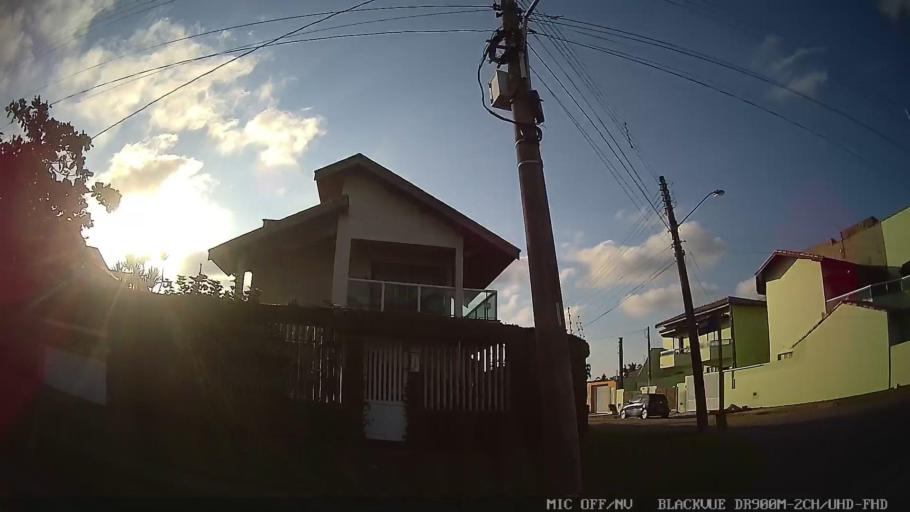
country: BR
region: Sao Paulo
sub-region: Peruibe
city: Peruibe
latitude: -24.3145
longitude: -46.9849
